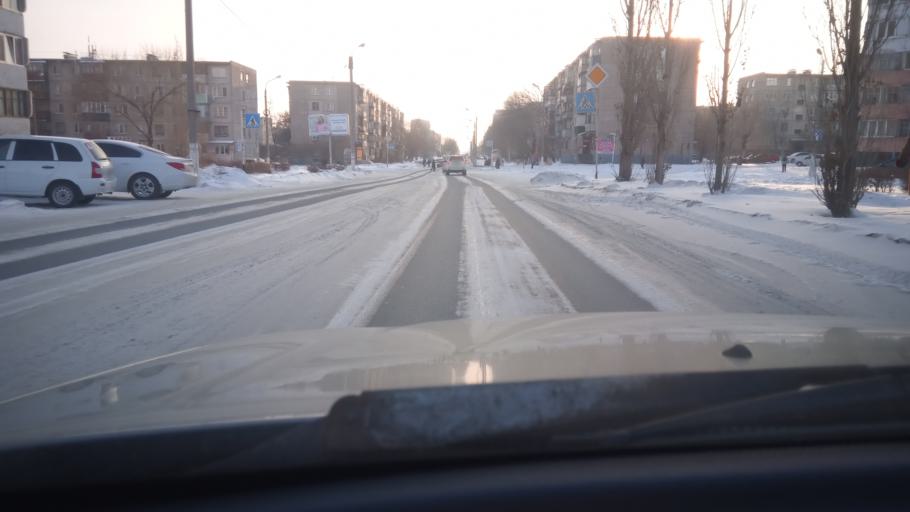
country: RU
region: Orenburg
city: Novotroitsk
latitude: 51.1899
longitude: 58.2815
